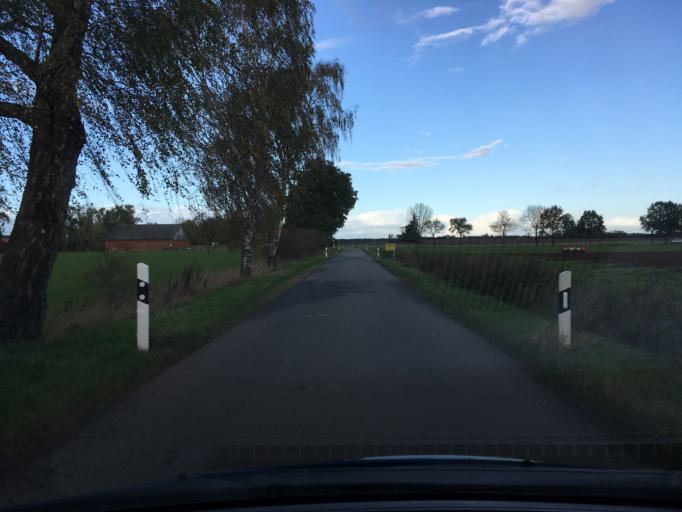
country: DE
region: Lower Saxony
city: Reinstorf
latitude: 53.2629
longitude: 10.5656
